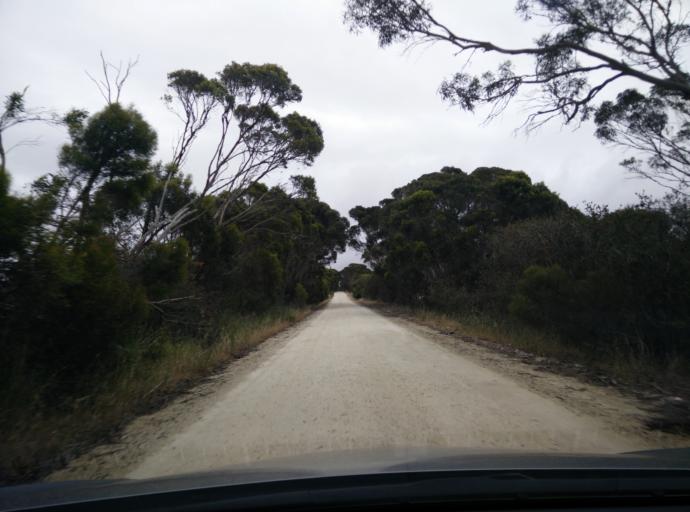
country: AU
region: South Australia
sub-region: Kangaroo Island
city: Kingscote
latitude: -35.8695
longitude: 137.5203
